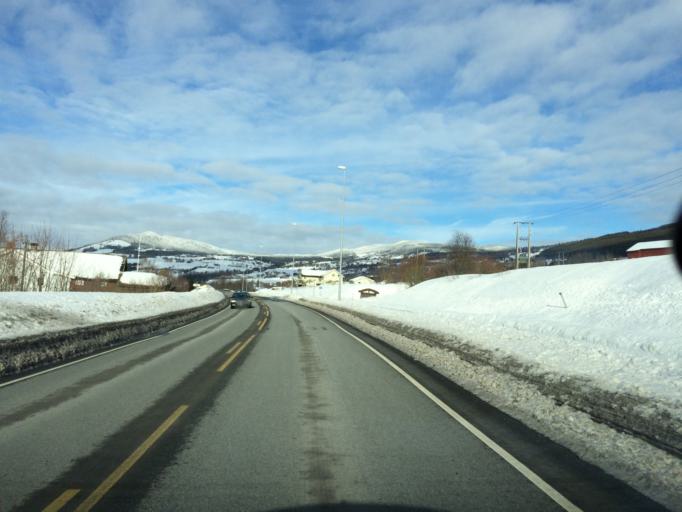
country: NO
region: Oppland
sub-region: Gausdal
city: Segalstad bru
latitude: 61.2011
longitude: 10.3052
